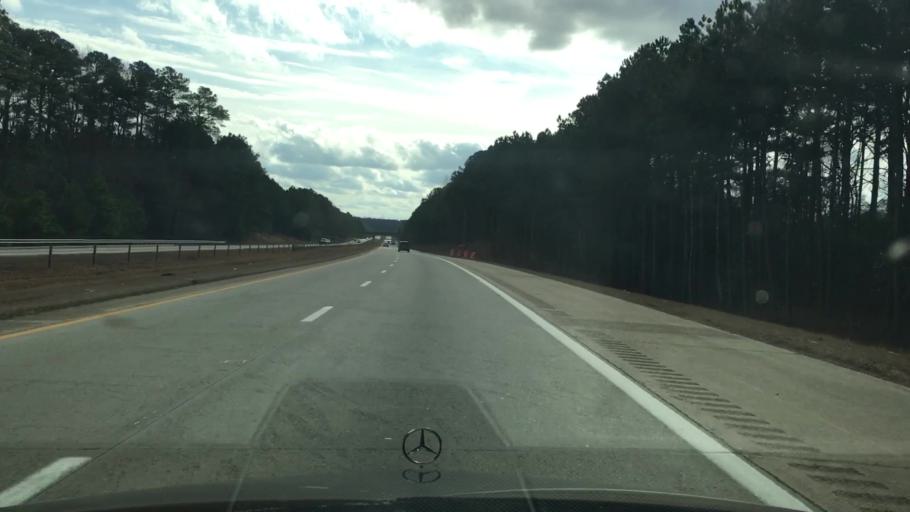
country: US
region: North Carolina
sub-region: Wake County
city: Garner
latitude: 35.5792
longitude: -78.5767
